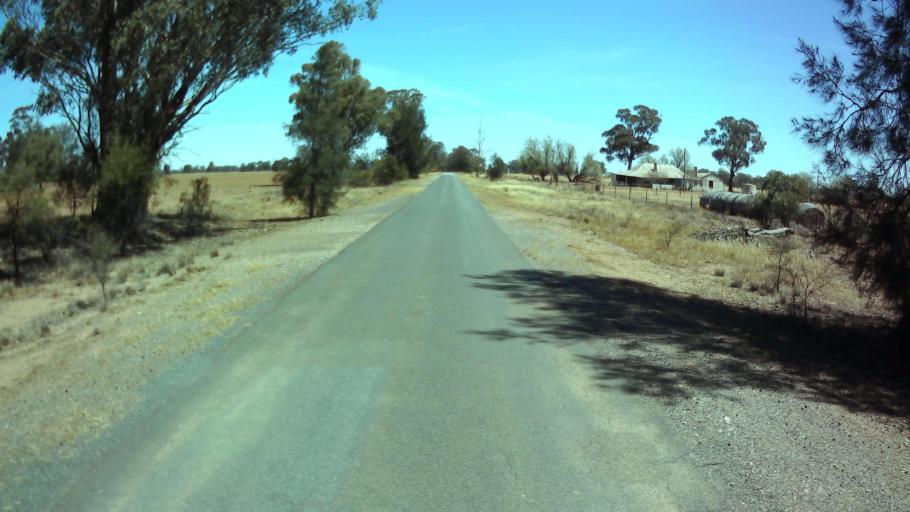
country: AU
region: New South Wales
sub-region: Weddin
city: Grenfell
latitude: -33.9044
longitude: 147.6857
